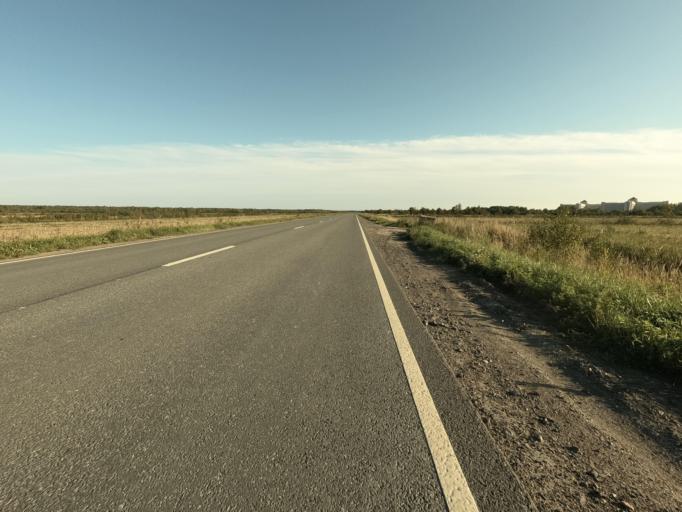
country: RU
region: St.-Petersburg
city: Sapernyy
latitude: 59.7523
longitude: 30.6356
